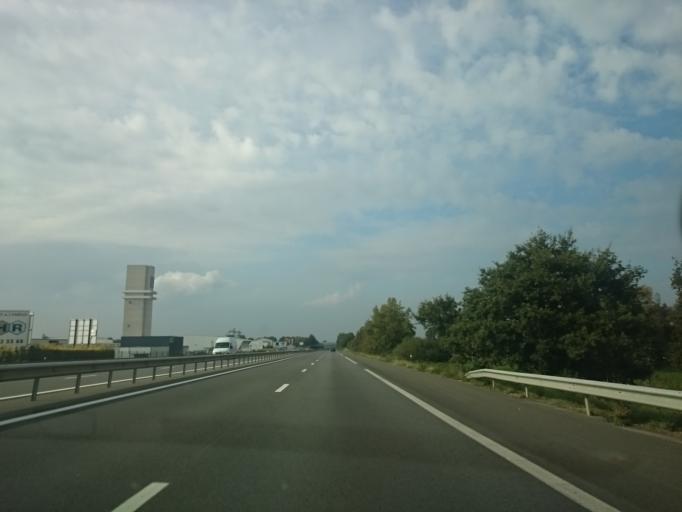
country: FR
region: Brittany
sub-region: Departement des Cotes-d'Armor
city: Broons
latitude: 48.3135
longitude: -2.2427
